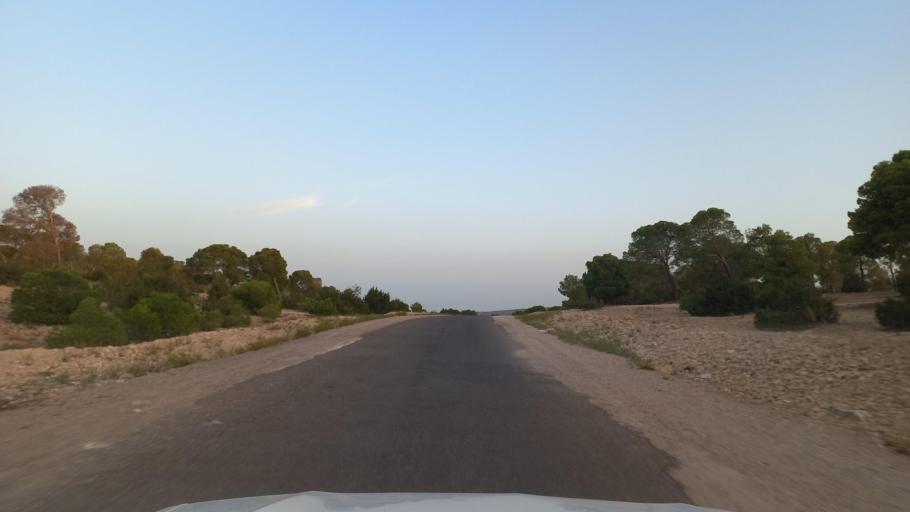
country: TN
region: Al Qasrayn
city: Sbiba
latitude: 35.4252
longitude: 8.9212
